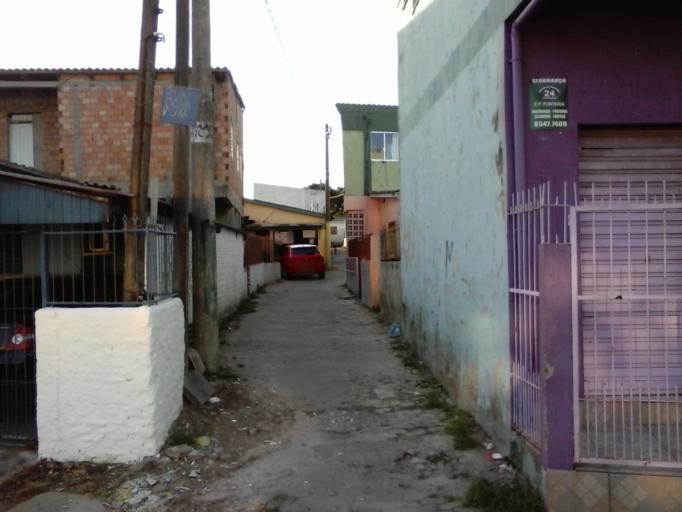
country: BR
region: Rio Grande do Sul
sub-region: Porto Alegre
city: Porto Alegre
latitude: -30.0447
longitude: -51.1497
